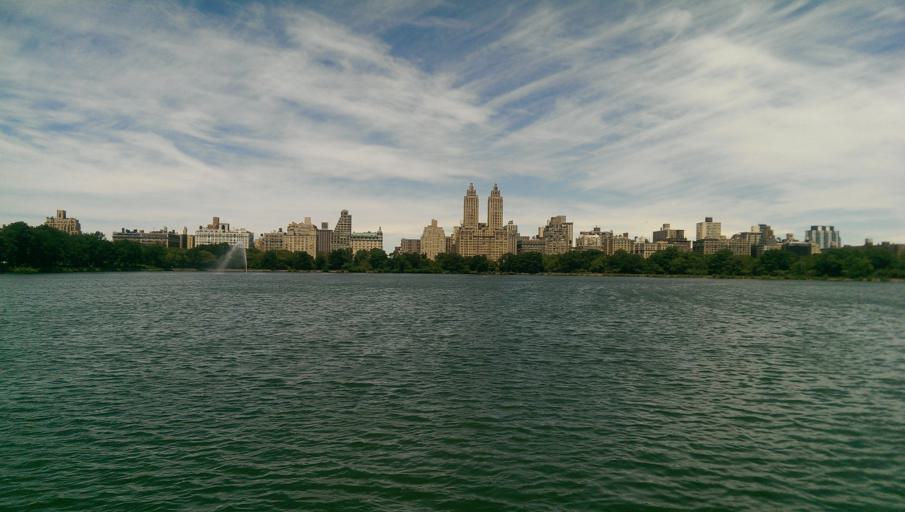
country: US
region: New York
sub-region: New York County
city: Manhattan
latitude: 40.7837
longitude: -73.9597
